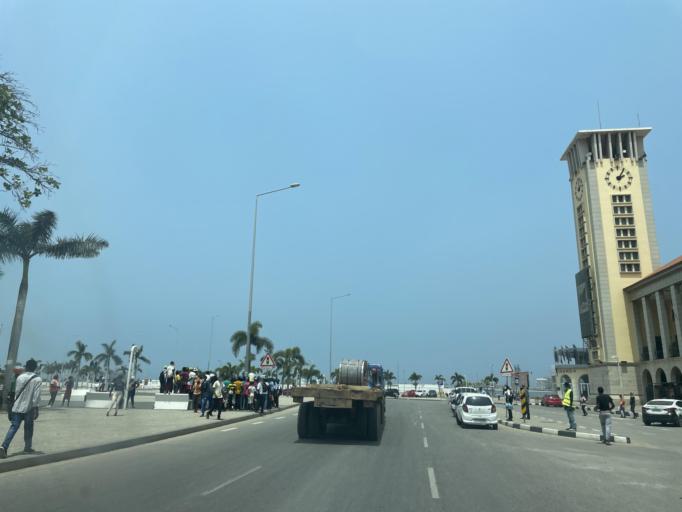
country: AO
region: Luanda
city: Luanda
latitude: -8.8025
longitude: 13.2428
